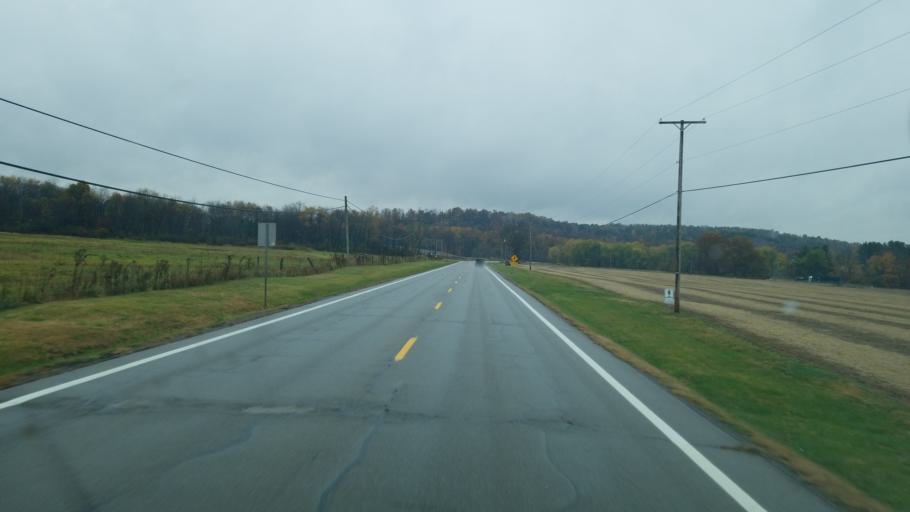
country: US
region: Ohio
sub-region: Coshocton County
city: Coshocton
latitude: 40.3288
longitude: -81.8607
